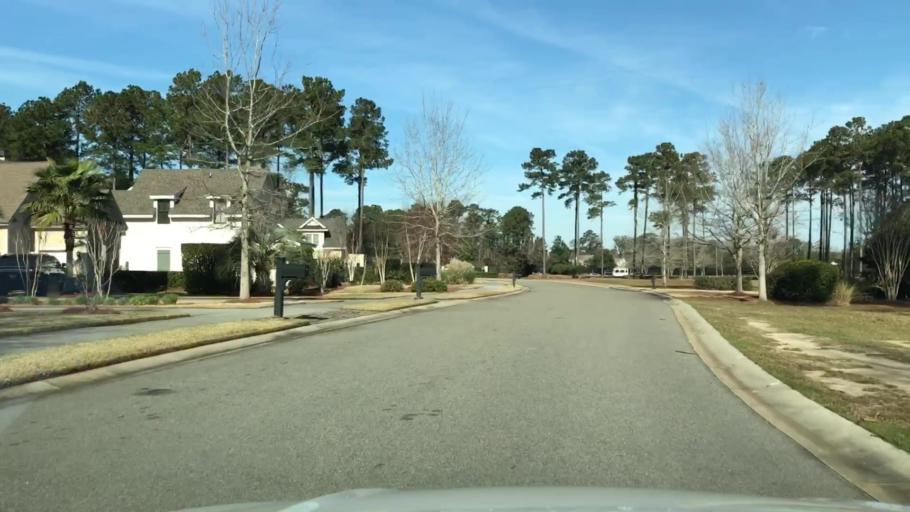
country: US
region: South Carolina
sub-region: Beaufort County
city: Bluffton
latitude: 32.2392
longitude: -80.9192
